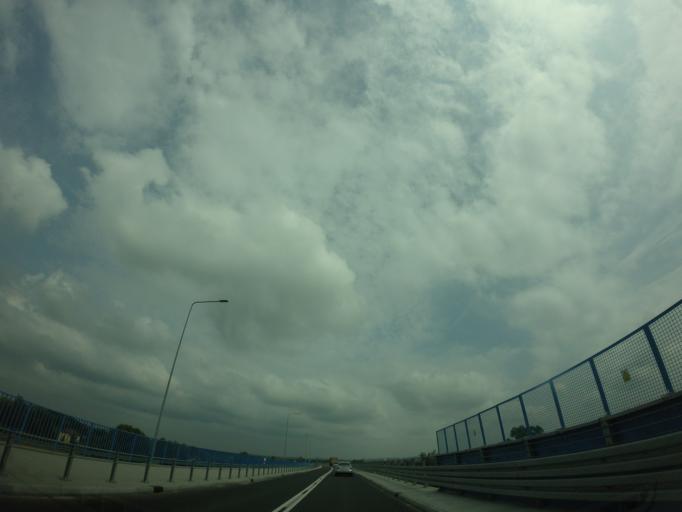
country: PL
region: Lesser Poland Voivodeship
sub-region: Powiat oswiecimski
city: Zaborze
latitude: 50.0464
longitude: 19.2565
